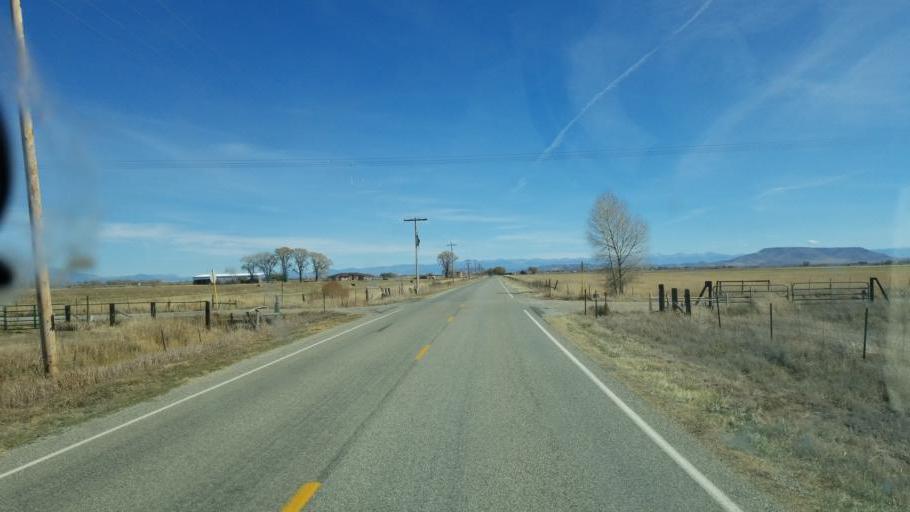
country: US
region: Colorado
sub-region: Conejos County
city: Conejos
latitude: 37.2837
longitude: -106.0203
